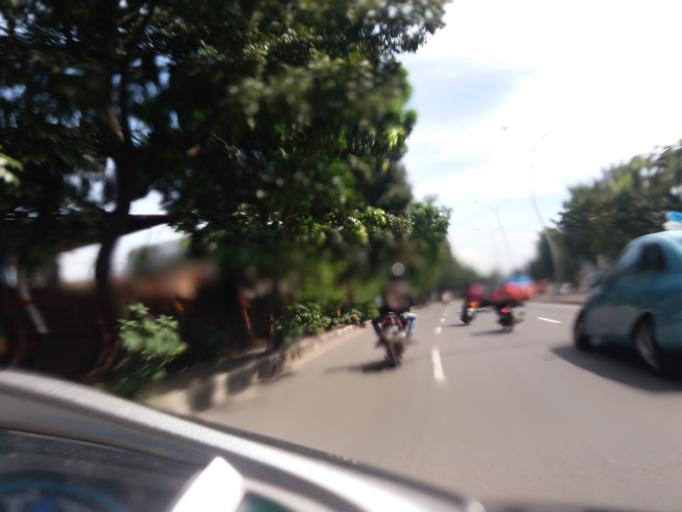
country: ID
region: West Java
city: Bandung
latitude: -6.9489
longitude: 107.6306
